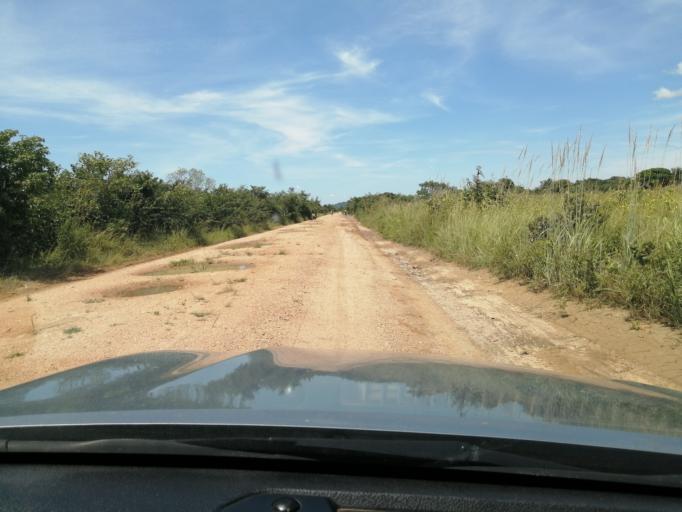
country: ZM
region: Central
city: Chibombo
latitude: -15.0444
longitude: 27.8244
